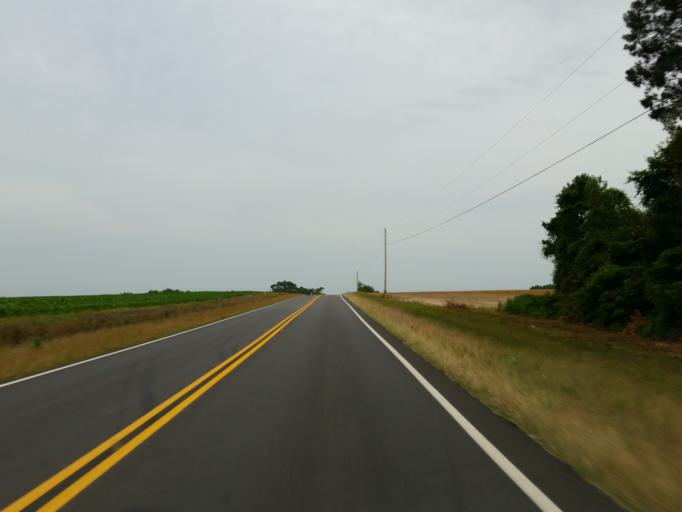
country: US
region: Georgia
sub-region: Dooly County
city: Unadilla
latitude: 32.2960
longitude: -83.7568
